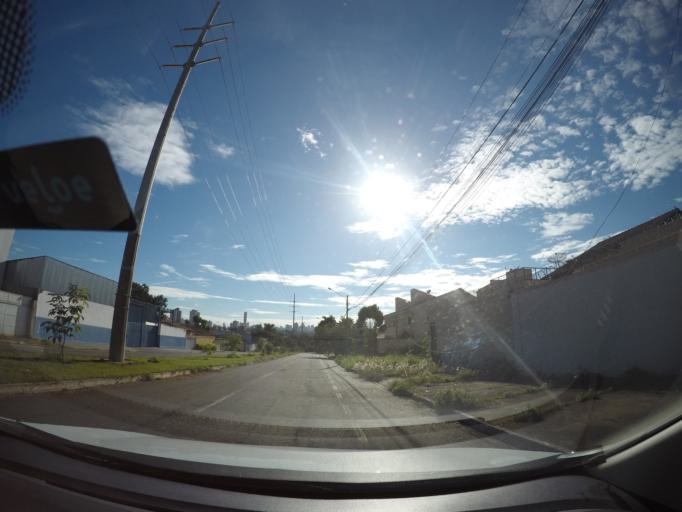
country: BR
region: Goias
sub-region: Goiania
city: Goiania
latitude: -16.7247
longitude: -49.2963
